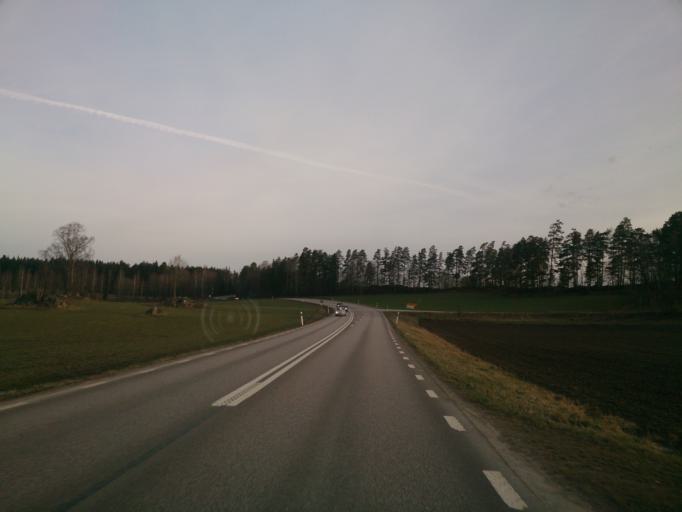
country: SE
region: OEstergoetland
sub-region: Atvidabergs Kommun
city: Atvidaberg
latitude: 58.2580
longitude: 15.9283
